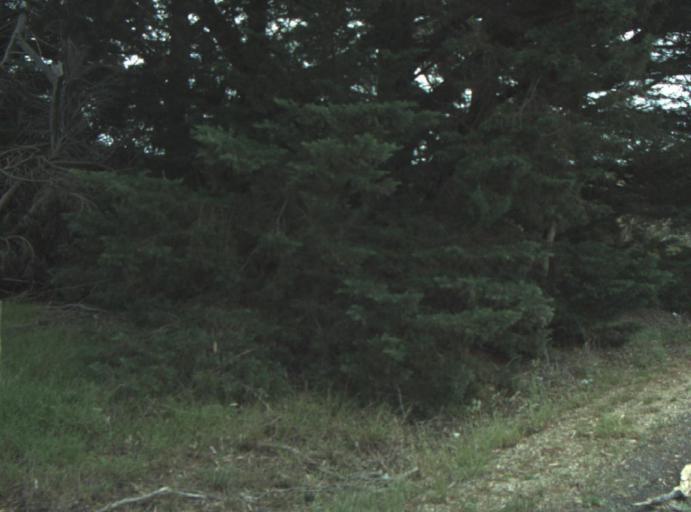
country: AU
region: Victoria
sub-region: Greater Geelong
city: Breakwater
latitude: -38.2211
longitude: 144.3510
